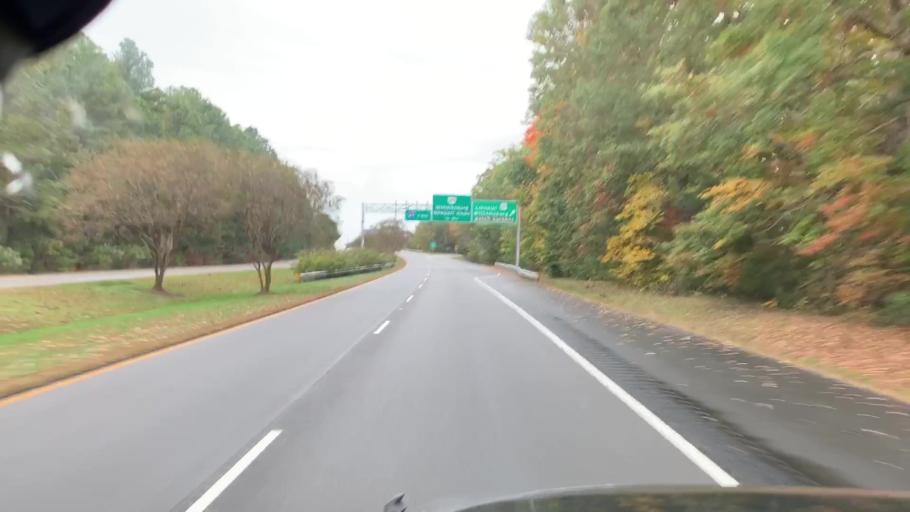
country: US
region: Virginia
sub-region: City of Williamsburg
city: Williamsburg
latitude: 37.2490
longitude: -76.6672
